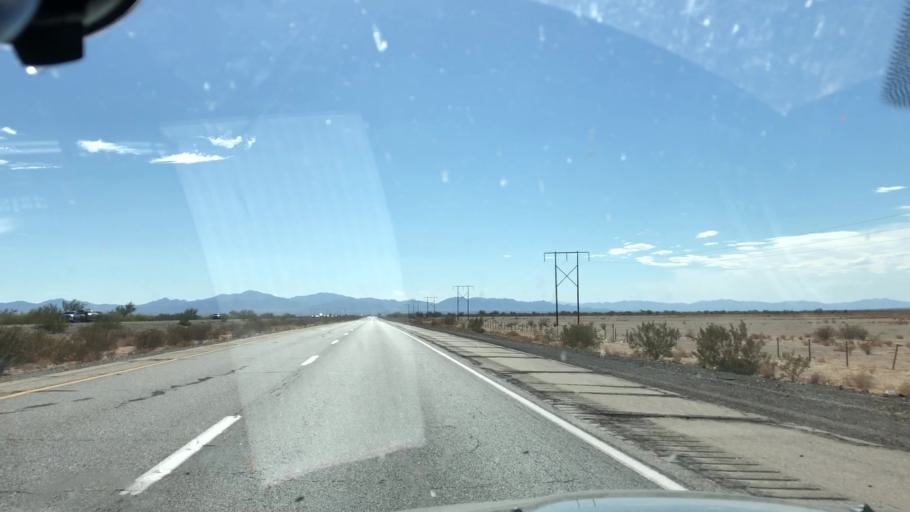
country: US
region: California
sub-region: Riverside County
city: Mesa Verde
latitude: 33.6063
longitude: -114.9616
